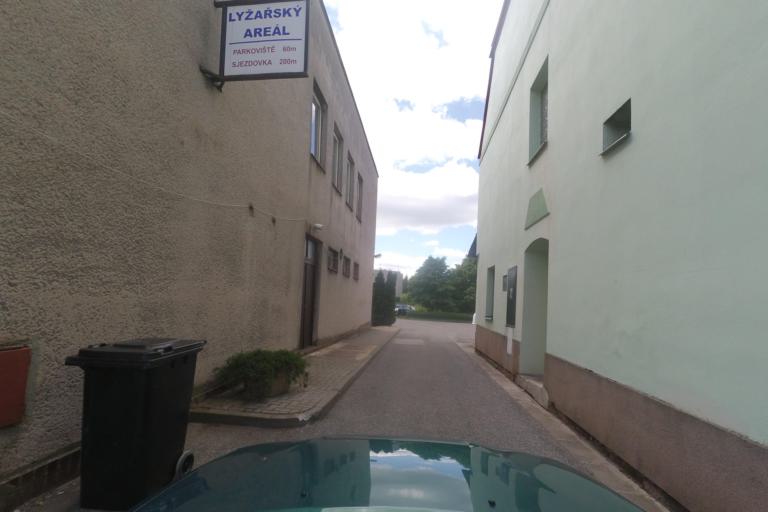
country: PL
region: Lower Silesian Voivodeship
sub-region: Powiat klodzki
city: Lewin Klodzki
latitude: 50.3572
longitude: 16.2435
